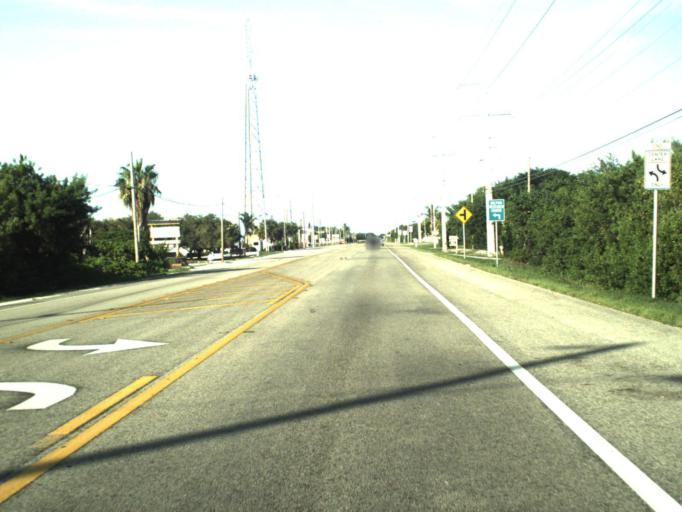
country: US
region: Florida
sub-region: Monroe County
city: Marathon
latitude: 24.7654
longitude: -80.9469
